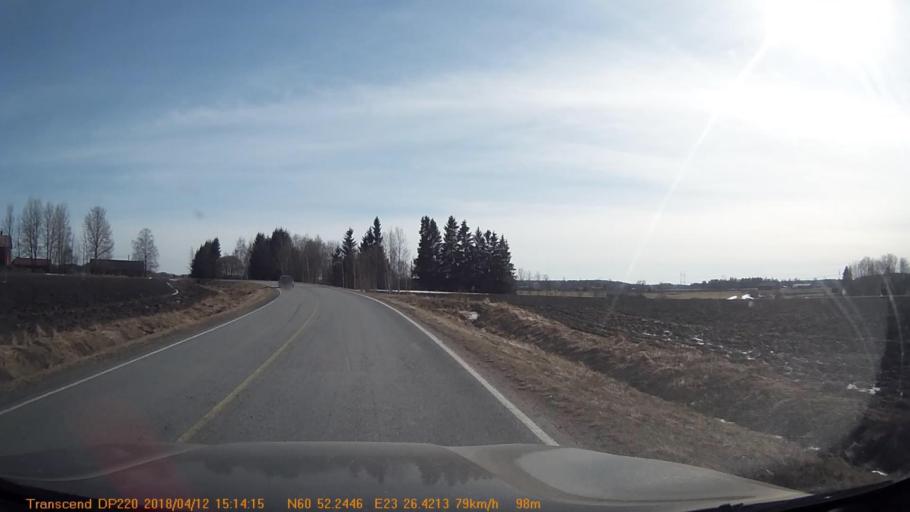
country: FI
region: Haeme
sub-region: Forssa
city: Jokioinen
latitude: 60.8704
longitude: 23.4405
